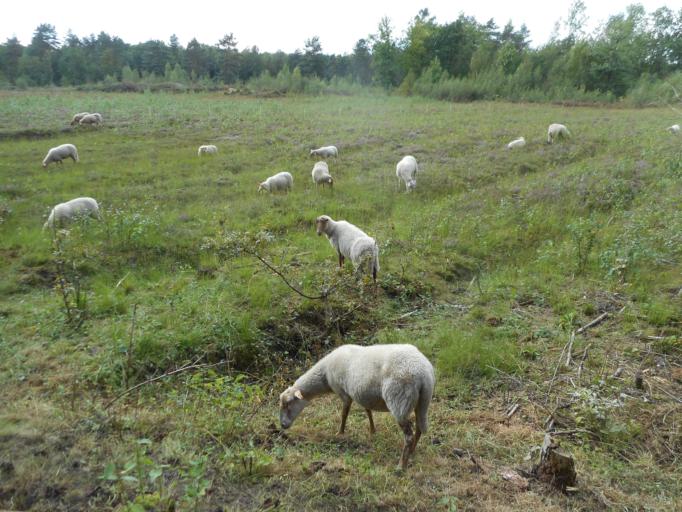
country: BE
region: Flanders
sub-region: Provincie Antwerpen
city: Lille
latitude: 51.2846
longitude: 4.8192
